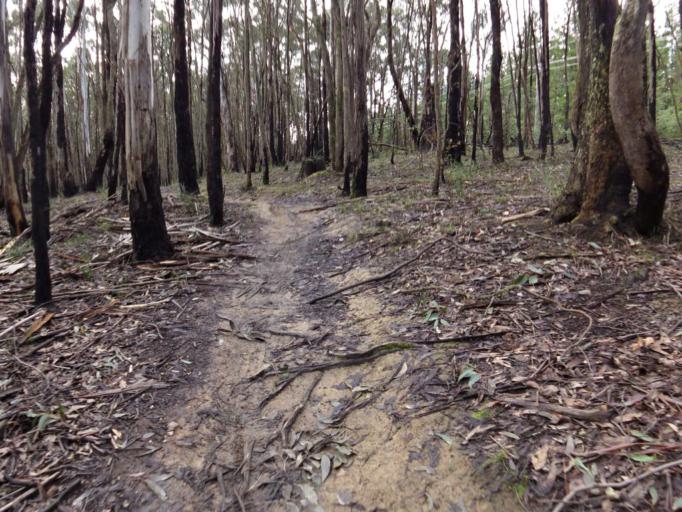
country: AU
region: Victoria
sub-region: Moorabool
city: Bacchus Marsh
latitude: -37.4139
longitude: 144.4964
